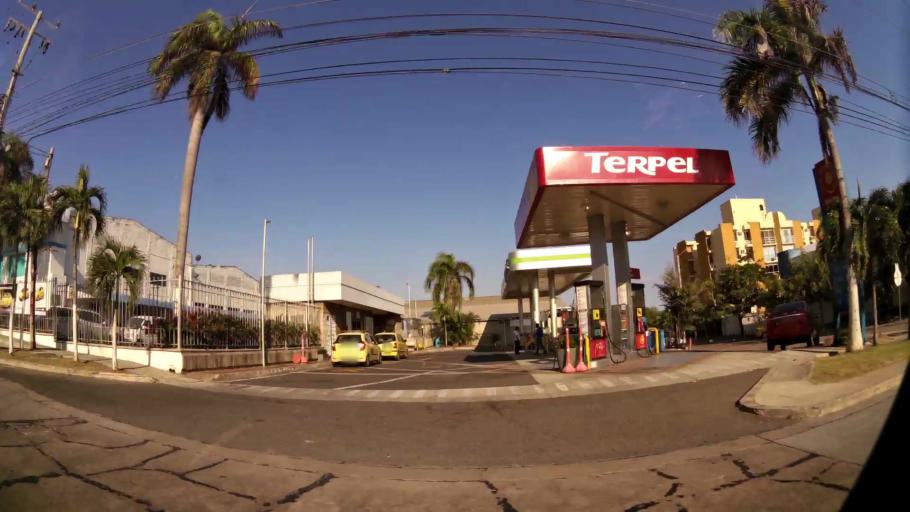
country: CO
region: Atlantico
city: Barranquilla
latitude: 11.0104
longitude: -74.7996
